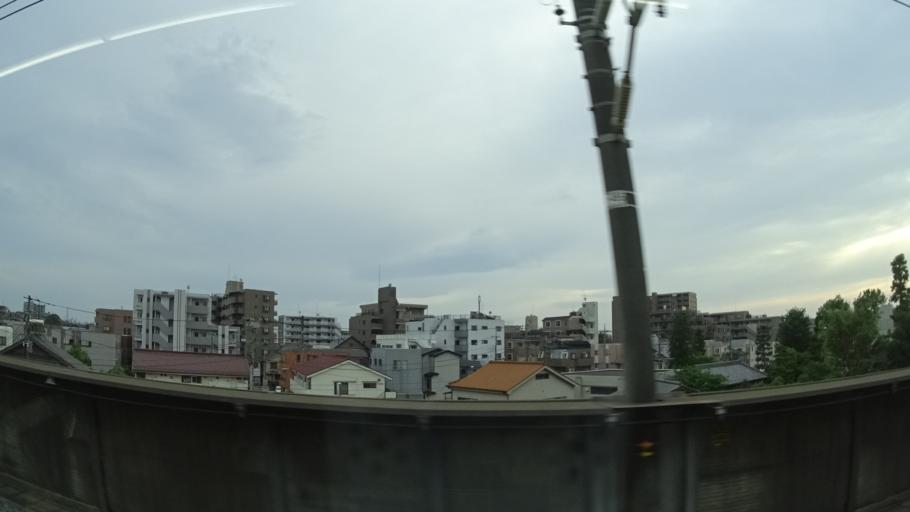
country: JP
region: Saitama
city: Shimotoda
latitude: 35.8125
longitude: 139.6727
